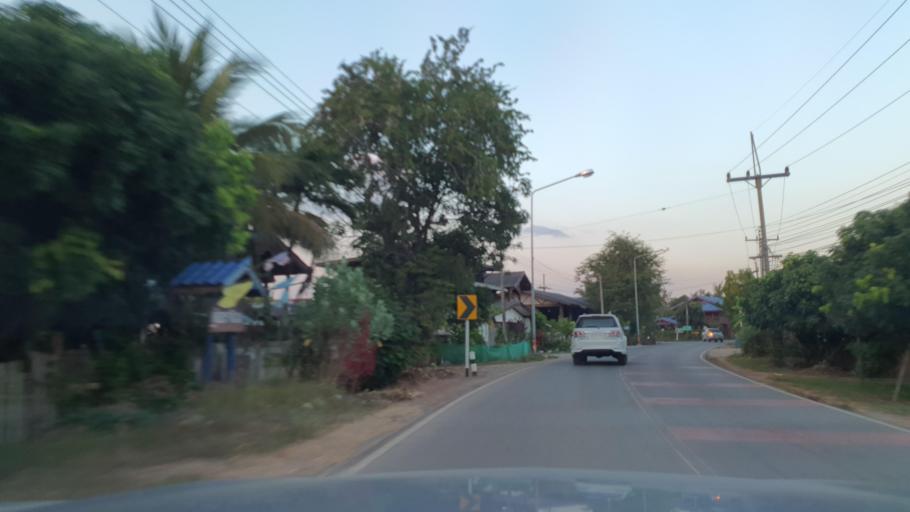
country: TH
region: Phayao
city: Dok Kham Tai
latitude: 19.0416
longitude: 100.0626
